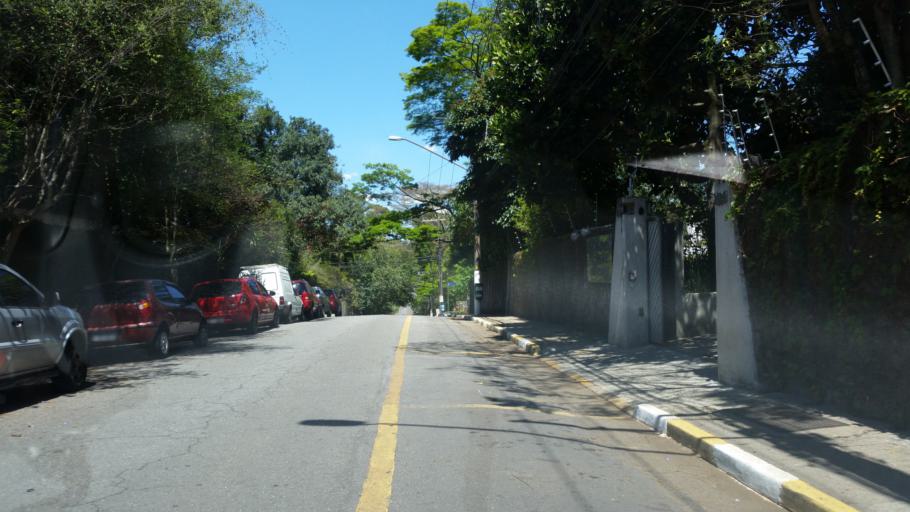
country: BR
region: Sao Paulo
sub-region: Diadema
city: Diadema
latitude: -23.6387
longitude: -46.6834
